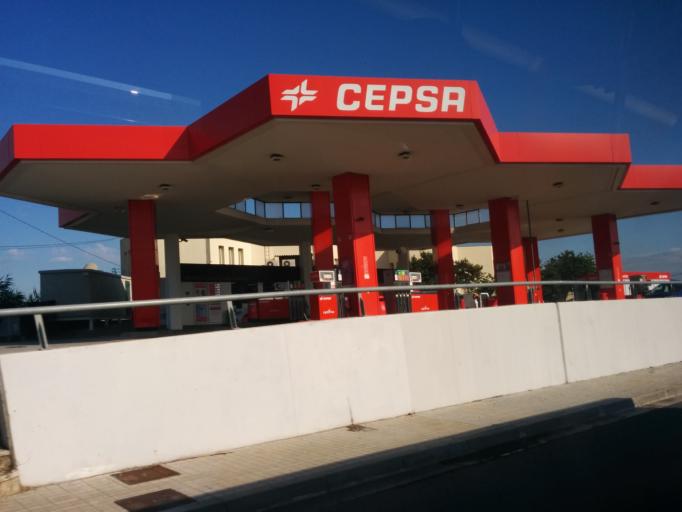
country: ES
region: Catalonia
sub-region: Provincia de Barcelona
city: El Prat de Llobregat
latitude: 41.3162
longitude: 2.0701
